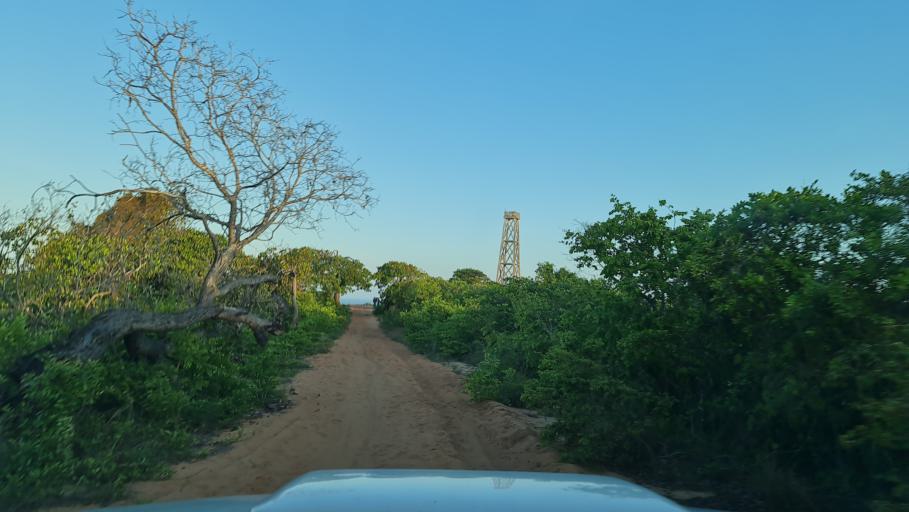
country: MZ
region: Nampula
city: Ilha de Mocambique
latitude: -15.6350
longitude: 40.4142
